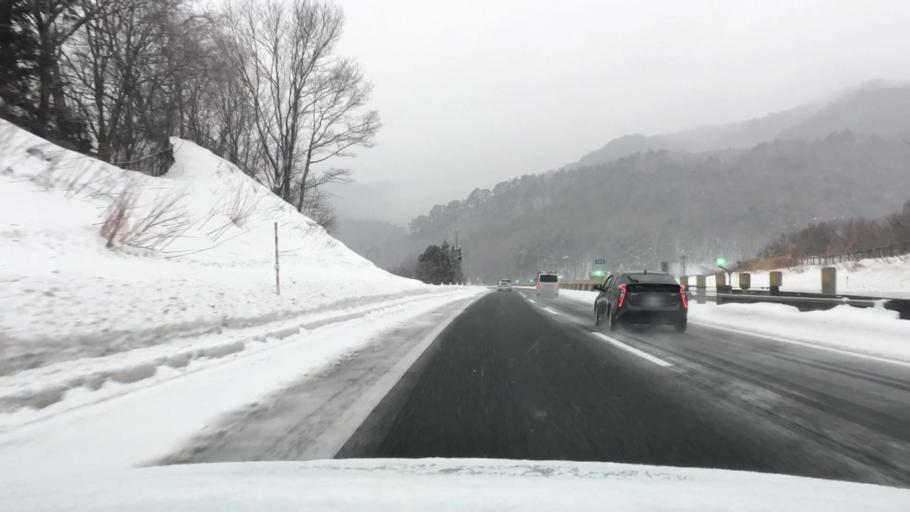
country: JP
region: Akita
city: Hanawa
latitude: 40.1131
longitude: 141.0343
